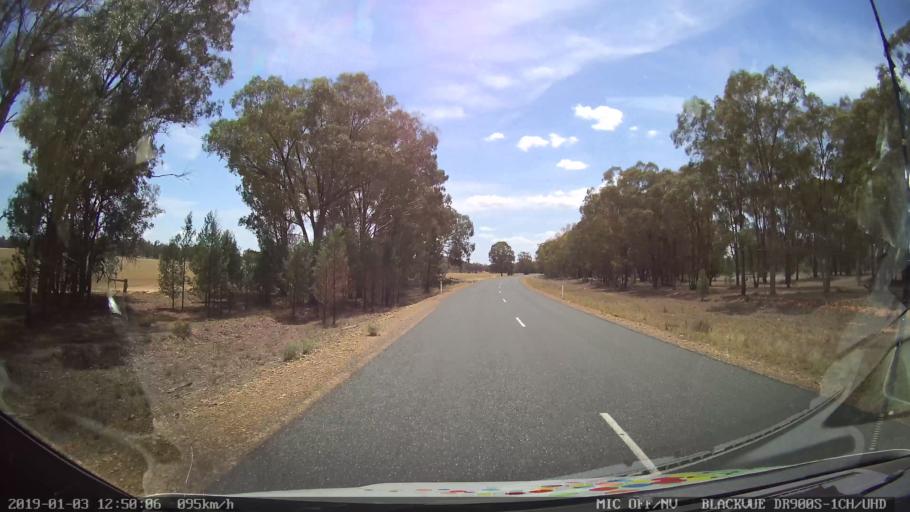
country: AU
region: New South Wales
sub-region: Weddin
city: Grenfell
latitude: -33.6952
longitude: 148.2664
